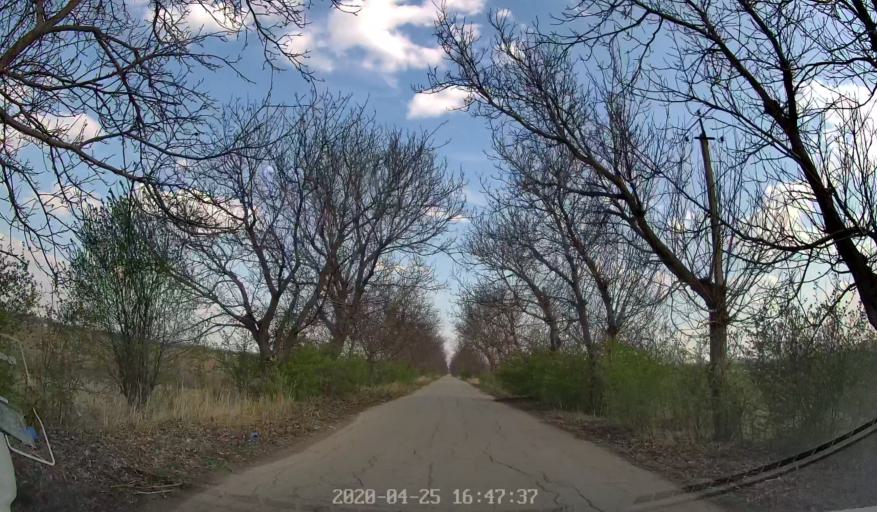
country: MD
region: Chisinau
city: Vadul lui Voda
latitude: 47.1358
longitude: 29.0743
